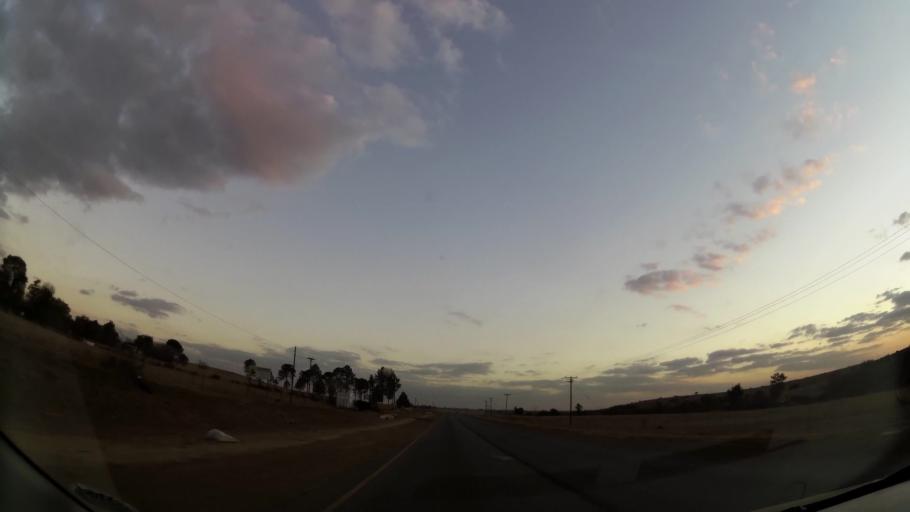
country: ZA
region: Gauteng
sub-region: West Rand District Municipality
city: Krugersdorp
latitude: -26.0459
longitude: 27.7176
